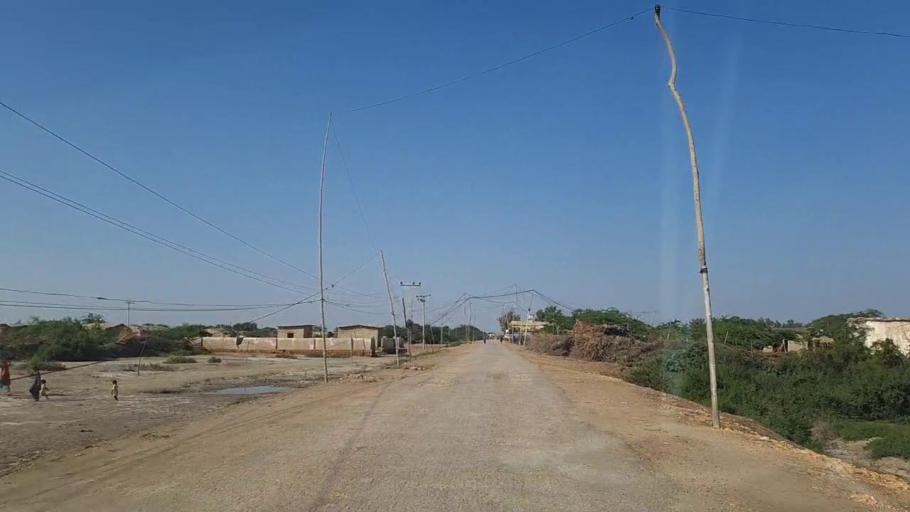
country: PK
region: Sindh
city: Thatta
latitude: 24.6165
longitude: 68.0287
